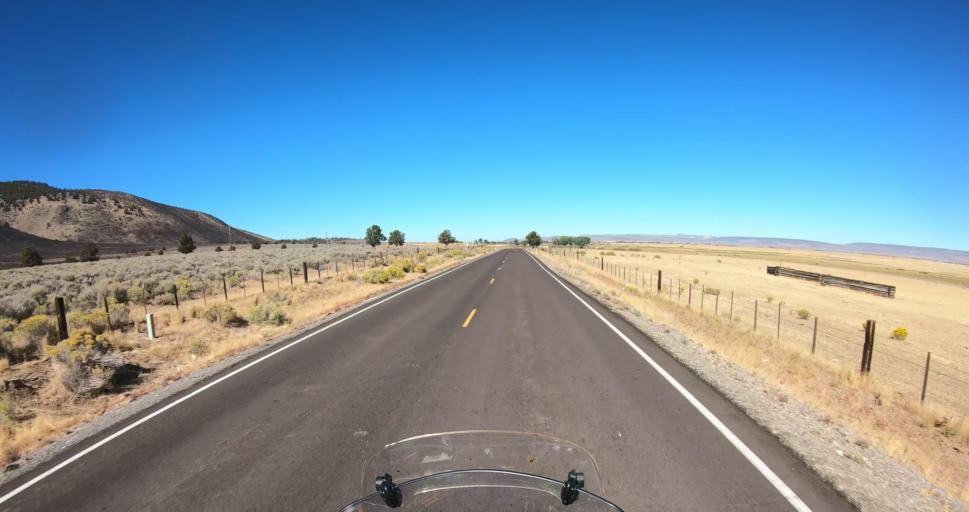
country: US
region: Oregon
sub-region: Lake County
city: Lakeview
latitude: 42.6492
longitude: -120.5217
